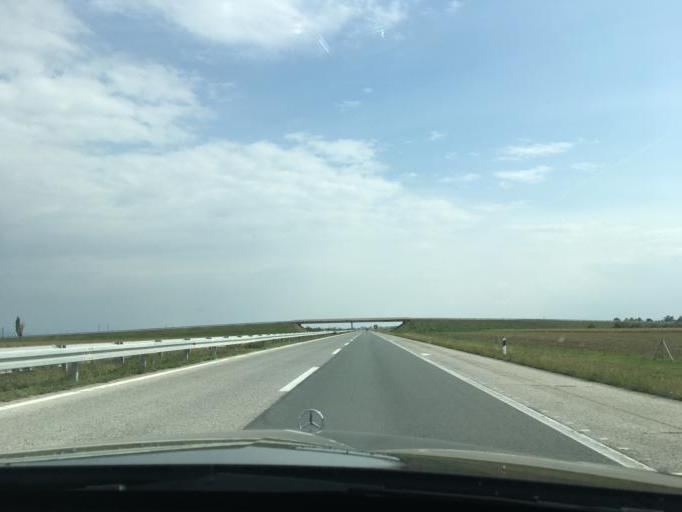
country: RS
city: Macvanska Mitrovica
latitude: 45.0177
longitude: 19.5400
